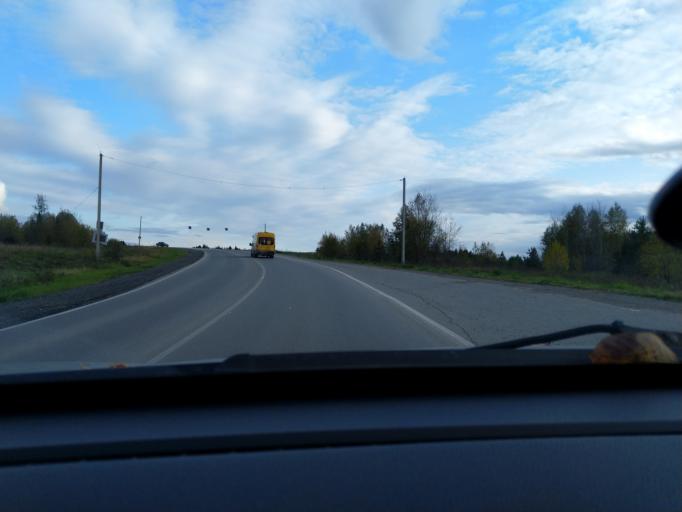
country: RU
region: Perm
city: Polazna
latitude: 58.2754
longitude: 56.4152
